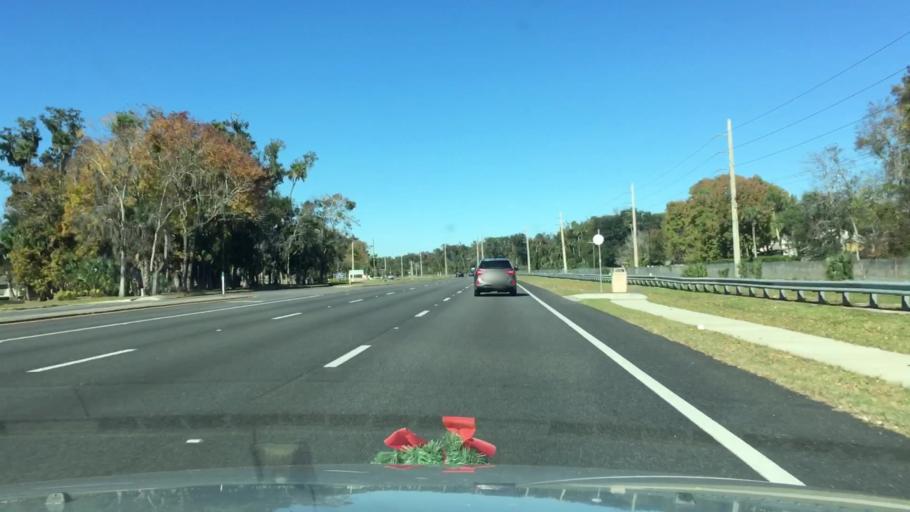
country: US
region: Florida
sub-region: Volusia County
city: Daytona Beach
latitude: 29.1843
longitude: -81.0300
